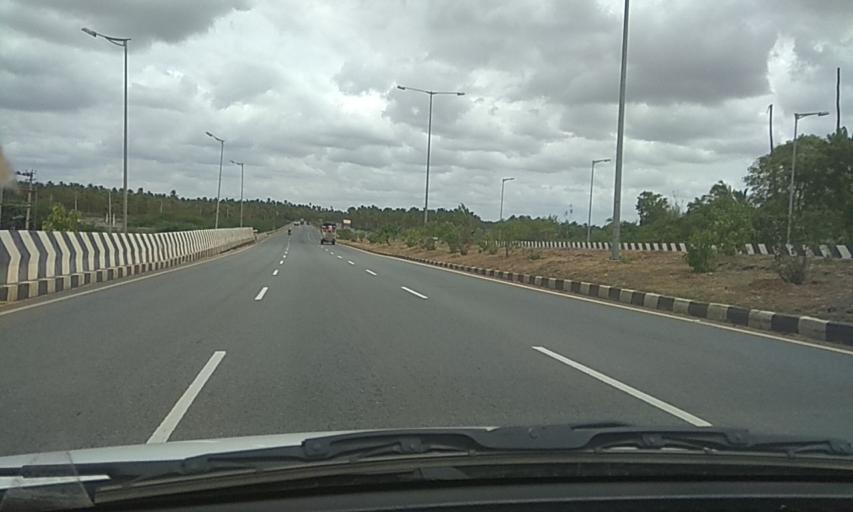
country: IN
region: Karnataka
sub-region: Chitradurga
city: Hiriyur
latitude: 13.9096
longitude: 76.6631
